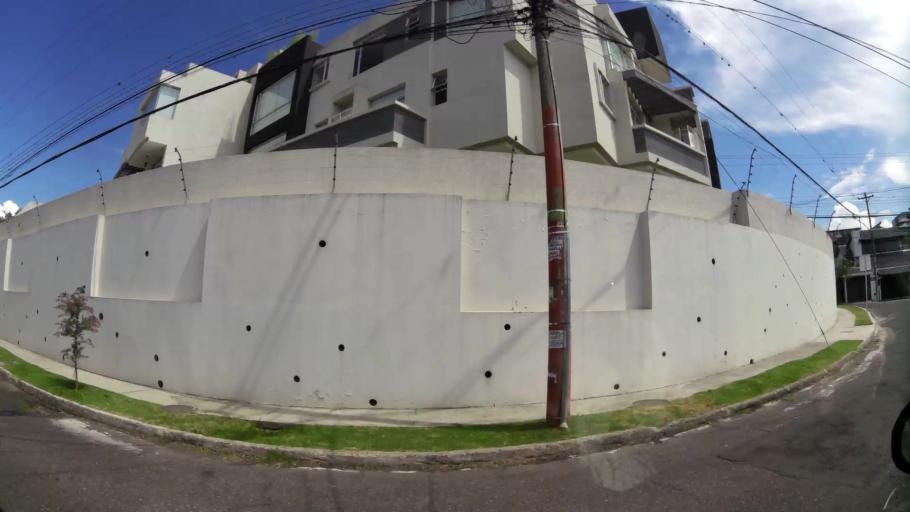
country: EC
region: Pichincha
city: Quito
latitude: -0.2138
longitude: -78.4322
